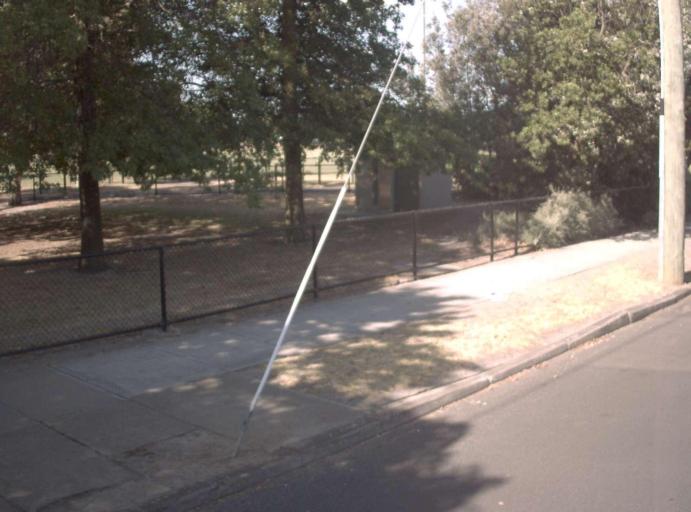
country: AU
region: Victoria
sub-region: Glen Eira
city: Glen Huntly
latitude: -37.8863
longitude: 145.0386
